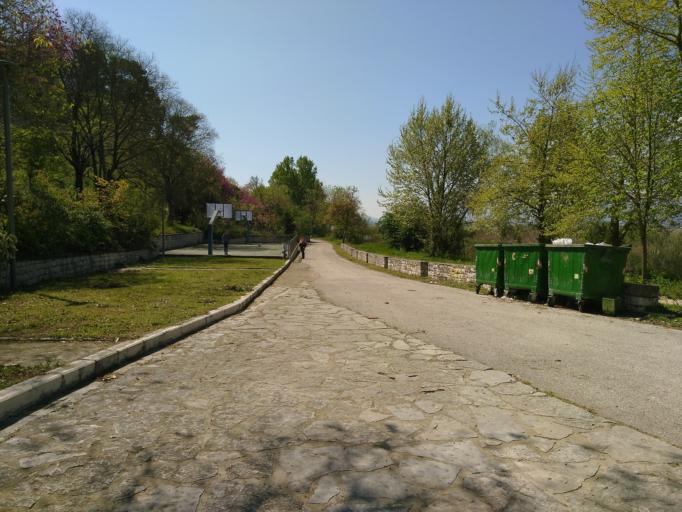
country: GR
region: Epirus
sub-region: Nomos Ioanninon
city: Ioannina
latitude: 39.6794
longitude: 20.8723
